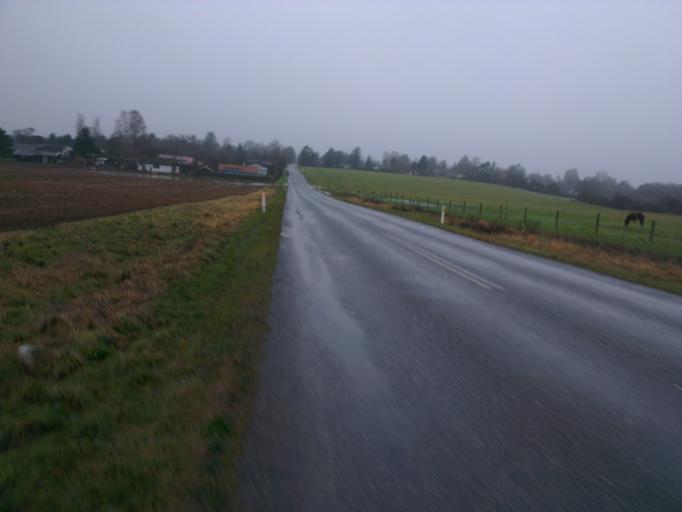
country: DK
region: Capital Region
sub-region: Frederikssund Kommune
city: Jaegerspris
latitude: 55.8332
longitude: 11.9799
